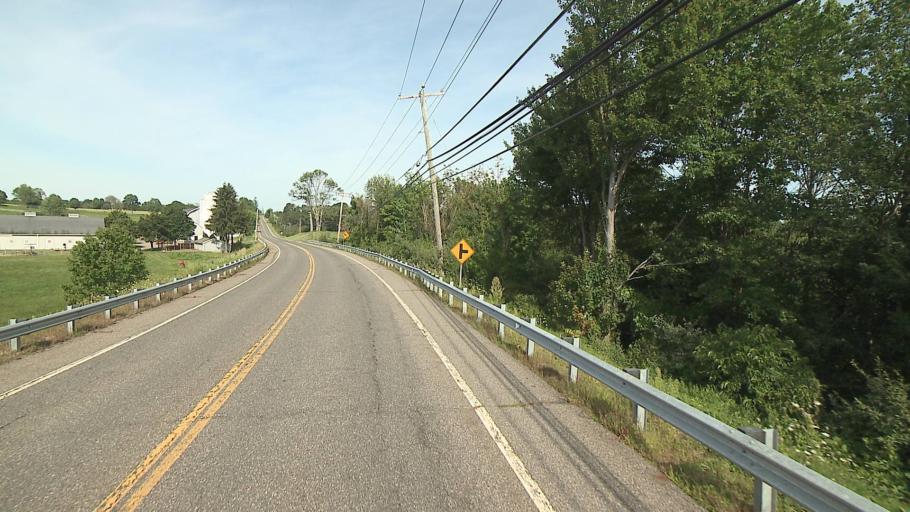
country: US
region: Connecticut
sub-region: Litchfield County
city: Thomaston
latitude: 41.7038
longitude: -73.1214
